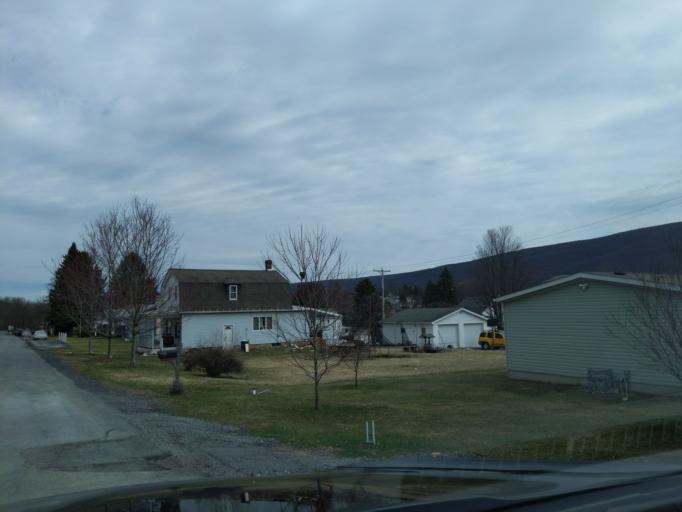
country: US
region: Pennsylvania
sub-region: Blair County
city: Altoona
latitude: 40.5236
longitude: -78.3769
